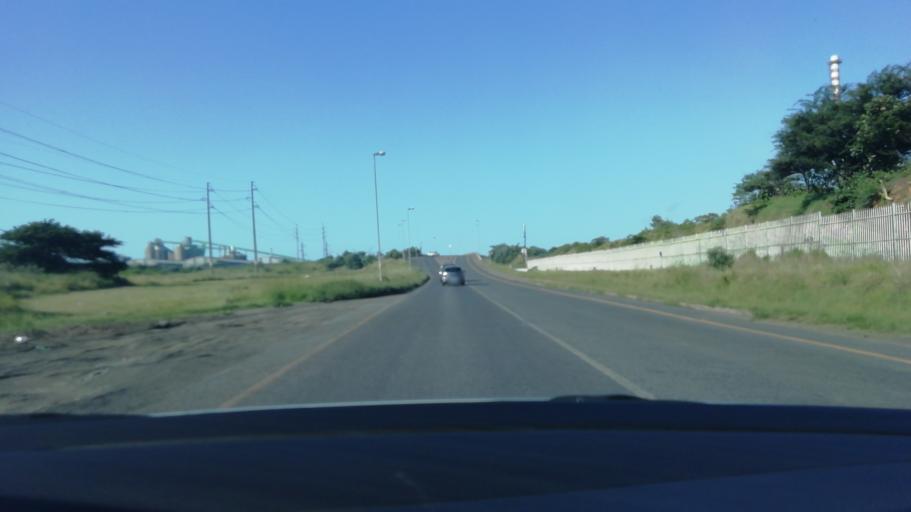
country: ZA
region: KwaZulu-Natal
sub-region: uThungulu District Municipality
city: Richards Bay
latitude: -28.7735
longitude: 32.0327
